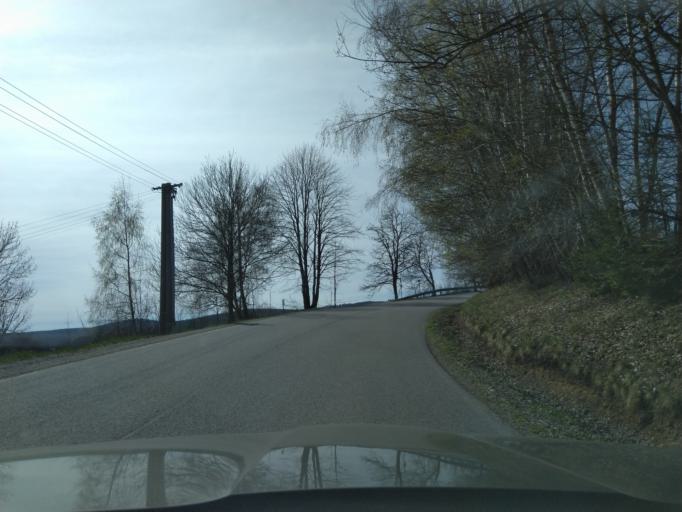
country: CZ
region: Jihocesky
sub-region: Okres Prachatice
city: Stachy
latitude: 49.0919
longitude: 13.6462
